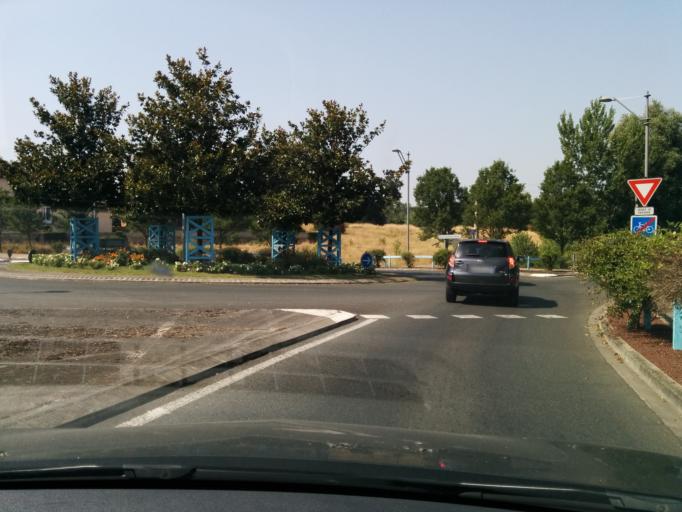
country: FR
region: Midi-Pyrenees
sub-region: Departement du Tarn
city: Albi
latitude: 43.9462
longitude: 2.1325
